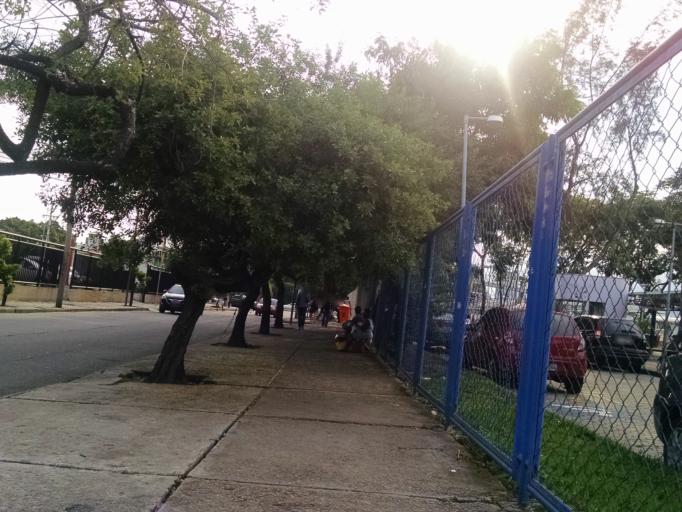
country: BR
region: Rio de Janeiro
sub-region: Rio De Janeiro
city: Rio de Janeiro
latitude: -22.9954
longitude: -43.3642
